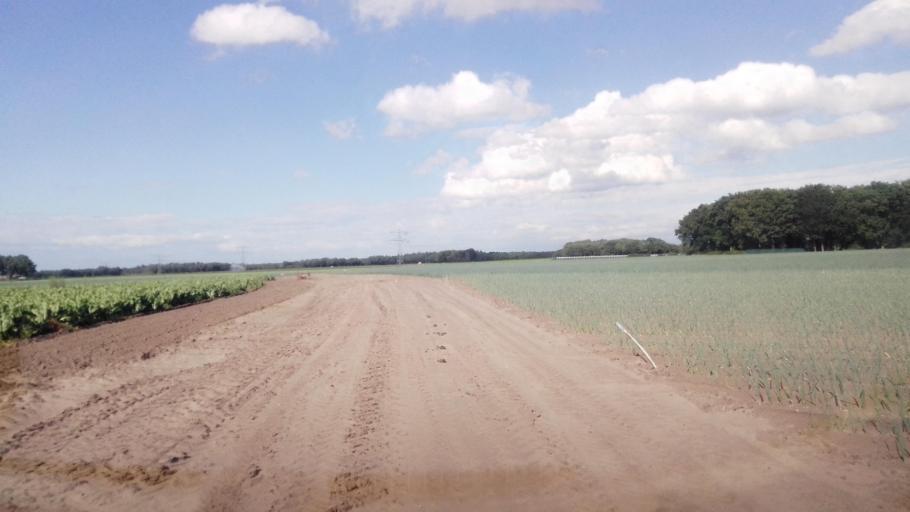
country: NL
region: Limburg
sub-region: Gemeente Peel en Maas
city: Maasbree
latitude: 51.3653
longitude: 6.0693
